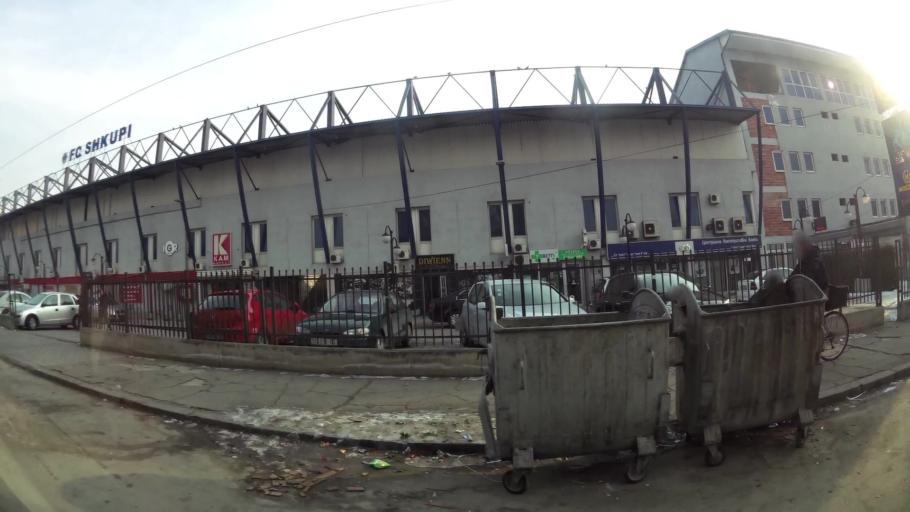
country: MK
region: Cair
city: Cair
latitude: 42.0153
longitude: 21.4436
